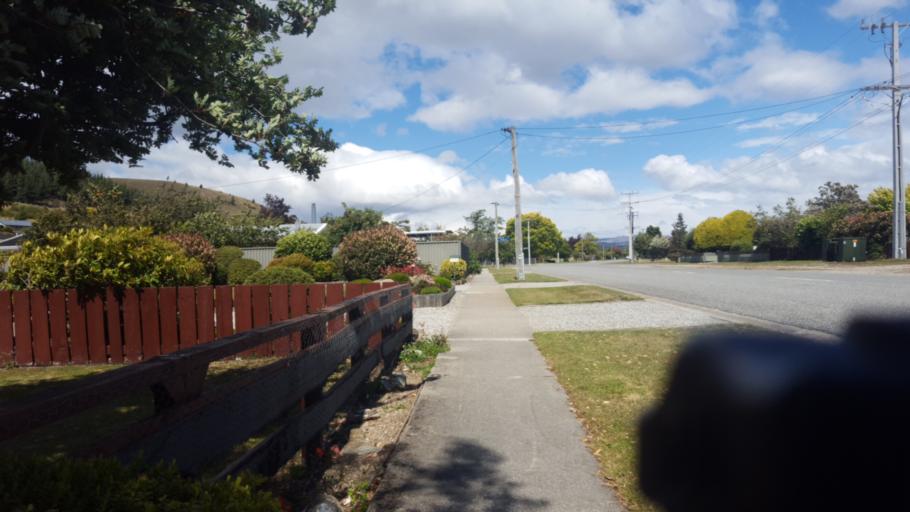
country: NZ
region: Otago
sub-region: Queenstown-Lakes District
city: Wanaka
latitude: -45.1877
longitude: 169.3236
